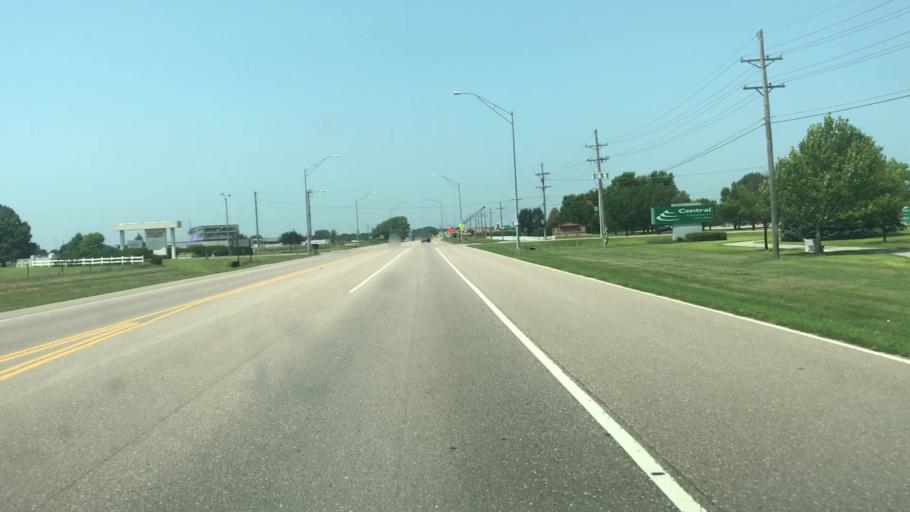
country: US
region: Nebraska
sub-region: Hall County
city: Grand Island
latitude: 40.8880
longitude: -98.3717
